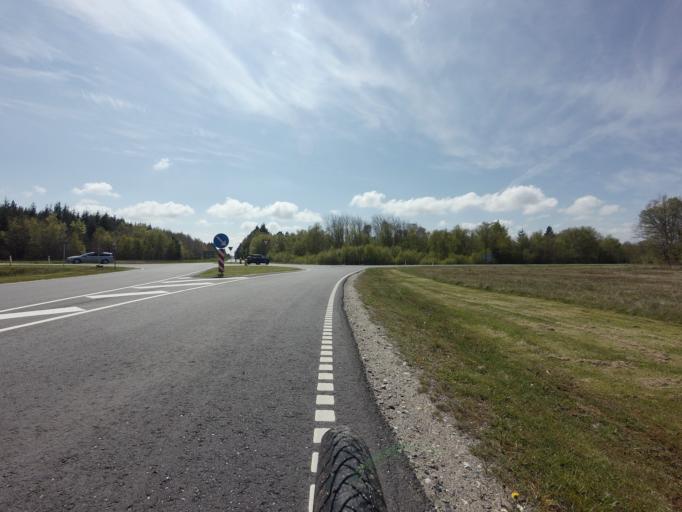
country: DK
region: North Denmark
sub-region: Jammerbugt Kommune
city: Brovst
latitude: 57.1630
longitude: 9.5752
